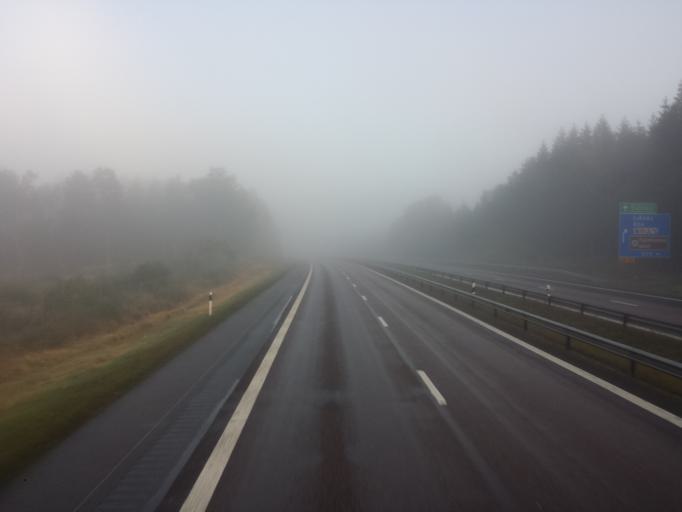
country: SE
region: Halland
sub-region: Kungsbacka Kommun
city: Fjaeras kyrkby
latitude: 57.4246
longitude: 12.1637
